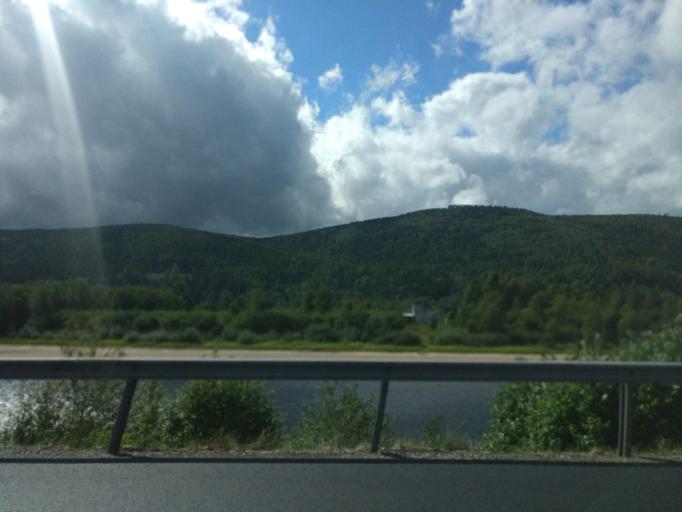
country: SE
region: Vaermland
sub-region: Hagfors Kommun
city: Ekshaerad
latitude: 60.3590
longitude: 13.3195
